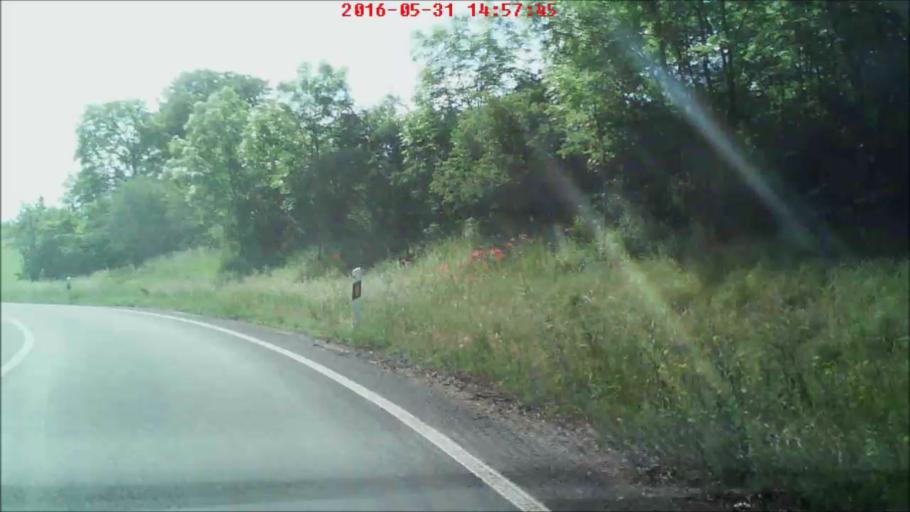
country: DE
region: Thuringia
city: Wundersleben
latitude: 51.1802
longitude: 11.0266
